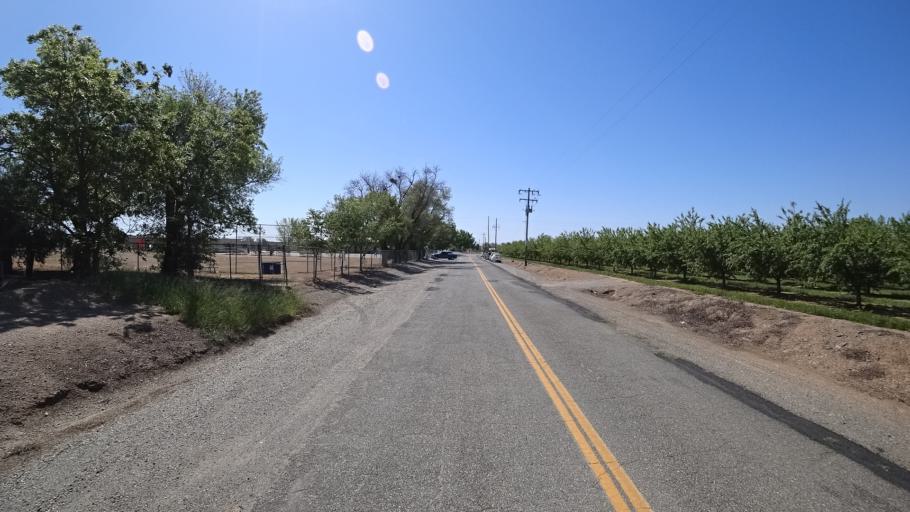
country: US
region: California
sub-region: Glenn County
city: Orland
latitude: 39.7703
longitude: -122.1596
